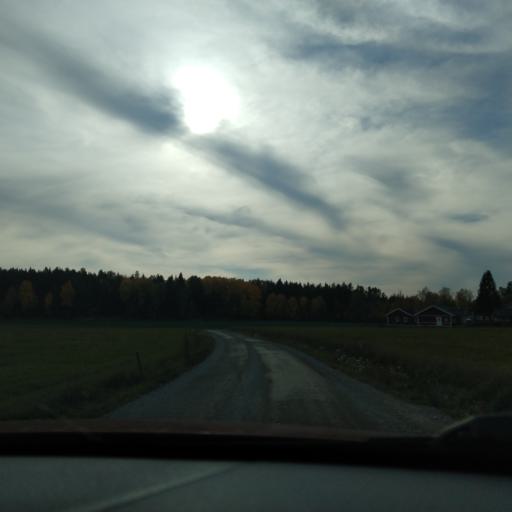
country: SE
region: Stockholm
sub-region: Vallentuna Kommun
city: Vallentuna
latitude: 59.5340
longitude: 18.0128
